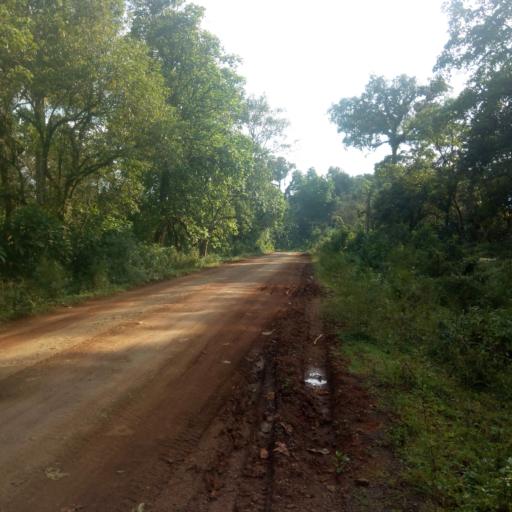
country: ET
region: Oromiya
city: Gore
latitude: 7.8853
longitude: 35.4857
